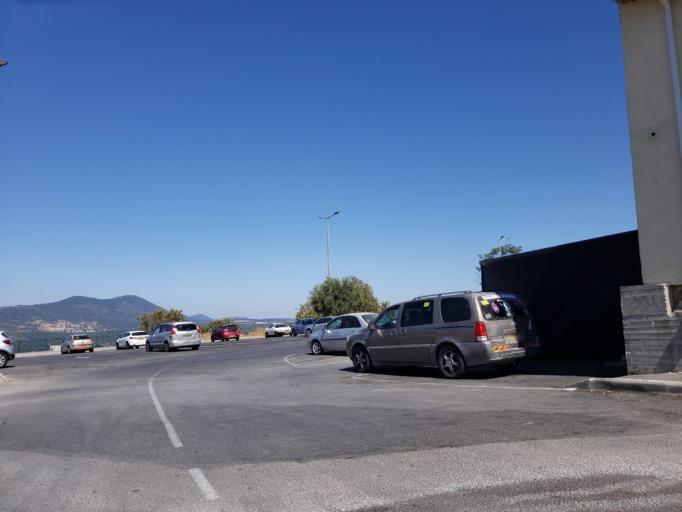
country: IL
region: Northern District
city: Safed
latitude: 32.9621
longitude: 35.4946
